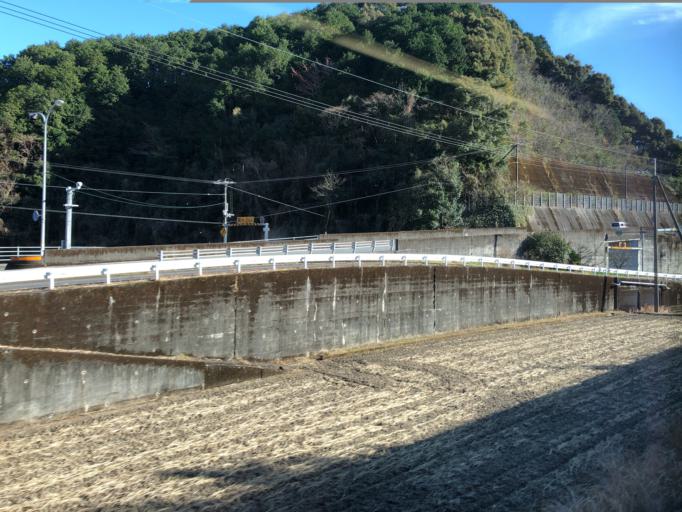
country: JP
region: Kochi
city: Nakamura
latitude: 33.1046
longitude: 133.0986
